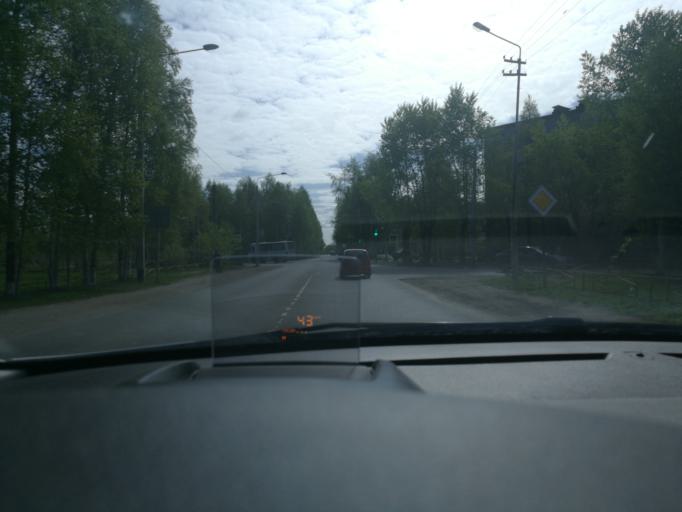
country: RU
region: Arkhangelskaya
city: Arkhangel'sk
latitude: 64.5928
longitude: 40.5883
